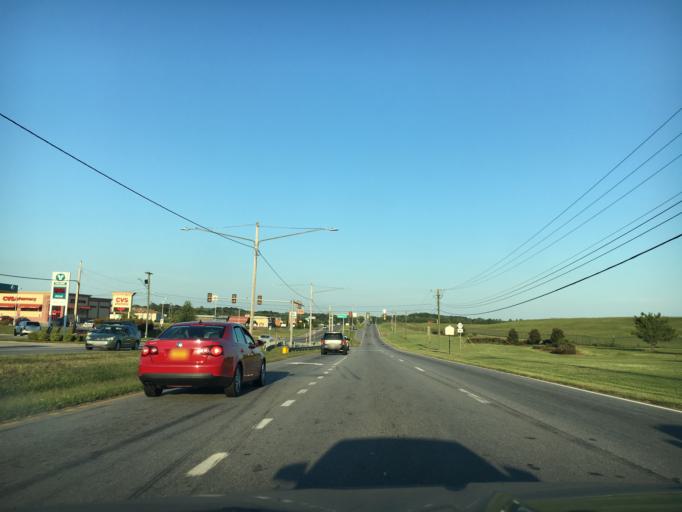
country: US
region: Virginia
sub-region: City of Danville
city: Danville
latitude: 36.5809
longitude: -79.3413
